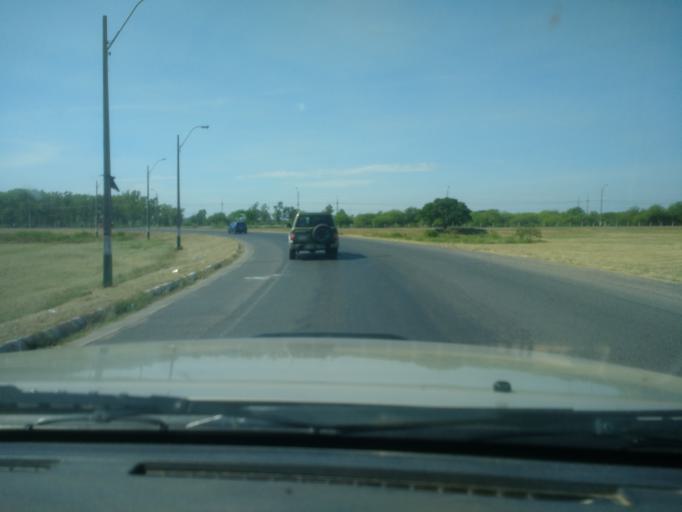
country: PY
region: Central
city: Colonia Mariano Roque Alonso
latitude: -25.1706
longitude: -57.5644
